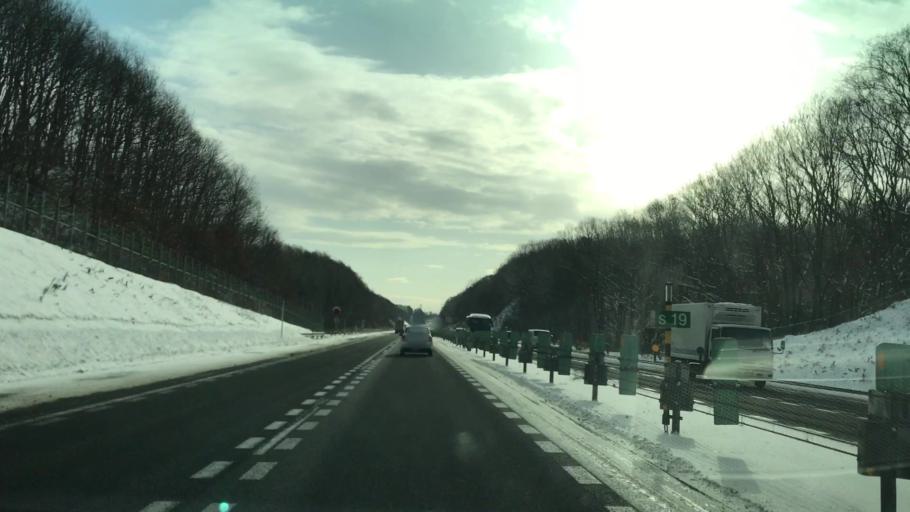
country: JP
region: Hokkaido
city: Kitahiroshima
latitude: 42.9318
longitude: 141.5310
